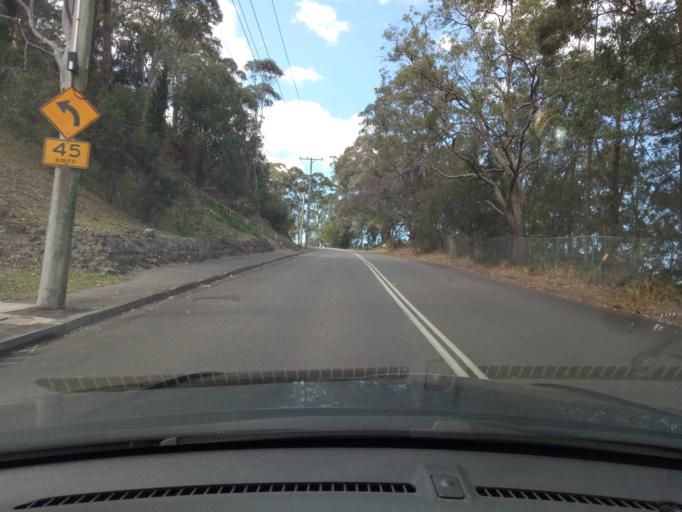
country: AU
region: New South Wales
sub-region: Gosford Shire
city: Point Clare
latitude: -33.4493
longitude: 151.3236
